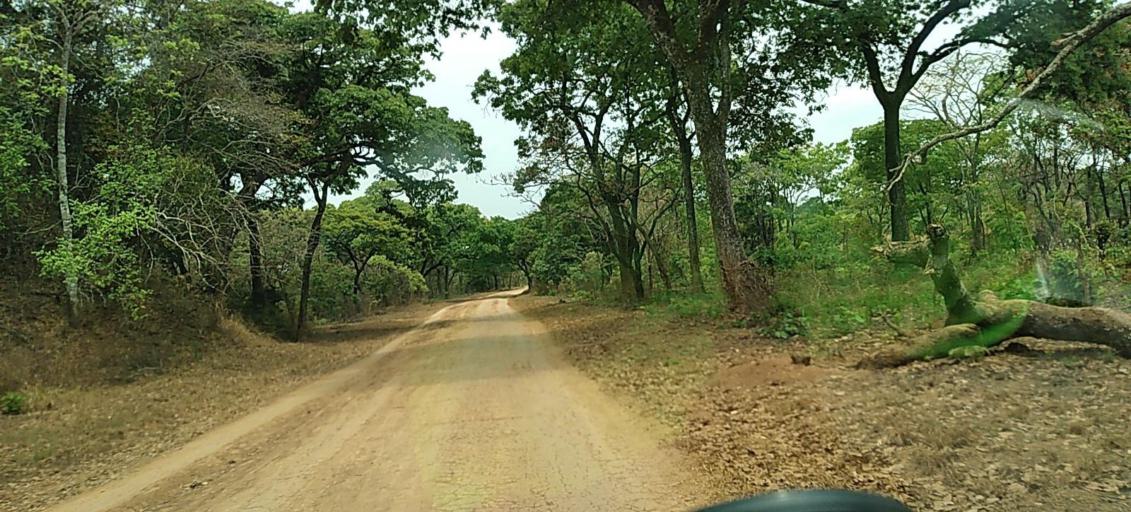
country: ZM
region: North-Western
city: Solwezi
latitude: -12.8217
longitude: 26.5369
